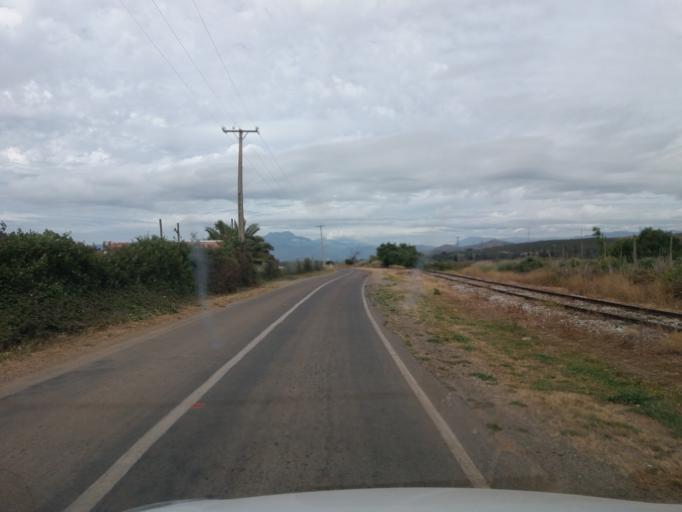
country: CL
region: Valparaiso
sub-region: Provincia de Marga Marga
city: Villa Alemana
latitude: -32.9163
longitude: -71.4131
